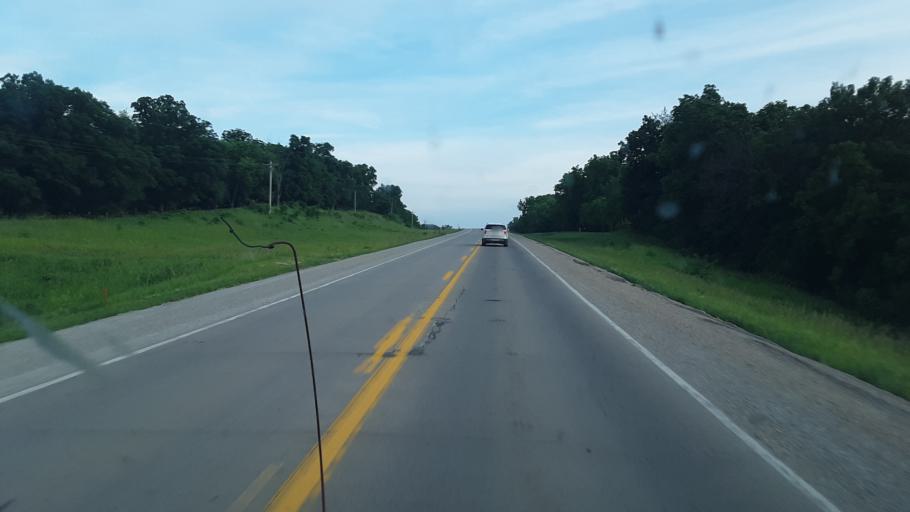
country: US
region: Iowa
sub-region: Benton County
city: Belle Plaine
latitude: 41.8387
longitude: -92.2786
